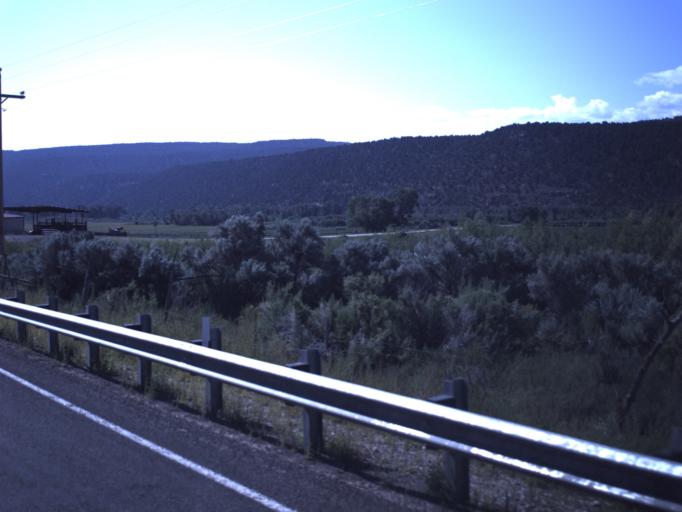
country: US
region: Utah
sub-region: Duchesne County
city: Duchesne
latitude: 40.3317
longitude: -110.6720
